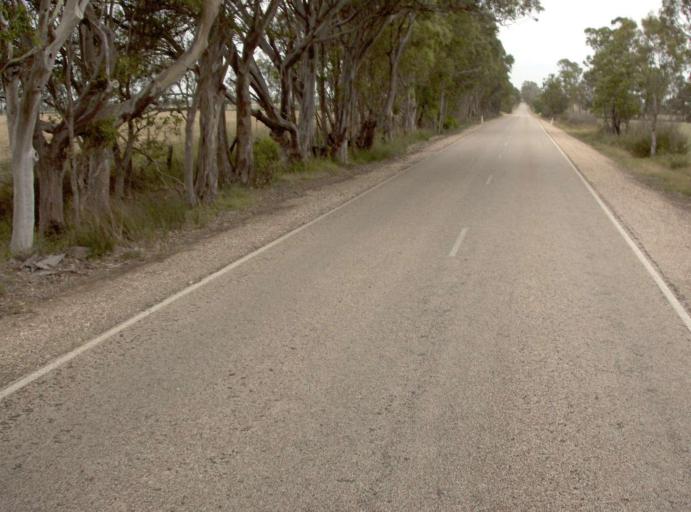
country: AU
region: Victoria
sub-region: East Gippsland
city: Bairnsdale
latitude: -37.8432
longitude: 147.4307
